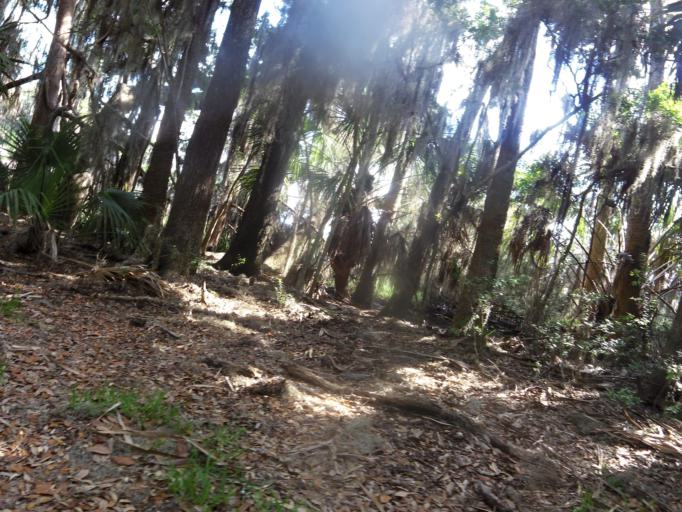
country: US
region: Florida
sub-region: Saint Johns County
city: Villano Beach
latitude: 30.0375
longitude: -81.3465
